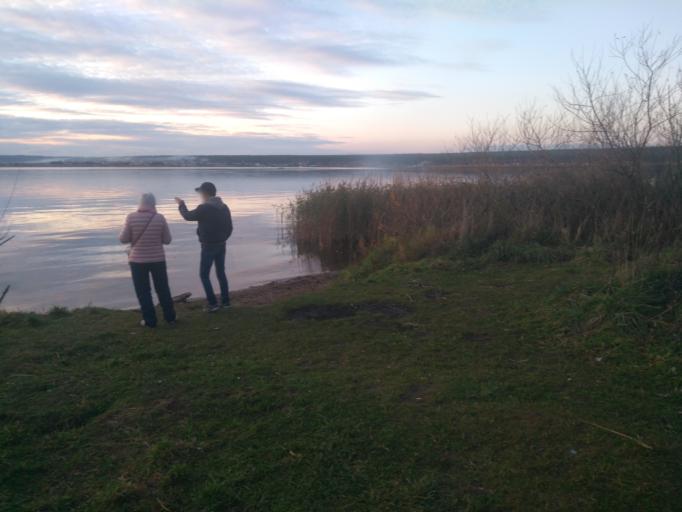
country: RU
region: Tatarstan
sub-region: Tukayevskiy Rayon
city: Naberezhnyye Chelny
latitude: 55.7676
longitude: 52.4014
